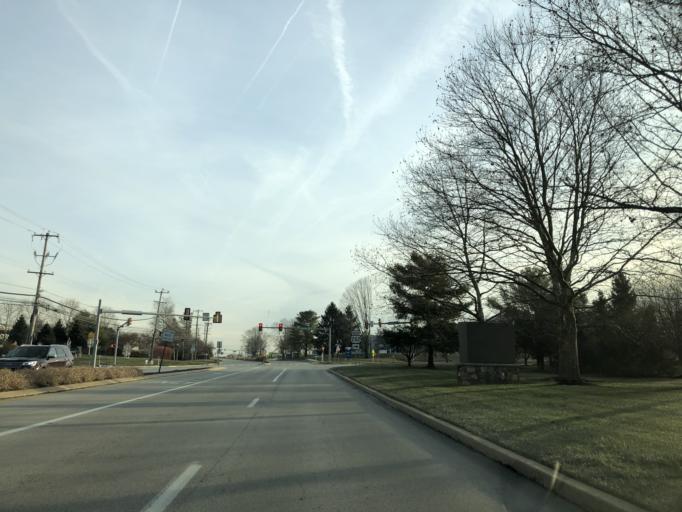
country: US
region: Pennsylvania
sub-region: Chester County
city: Malvern
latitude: 40.0544
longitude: -75.5221
